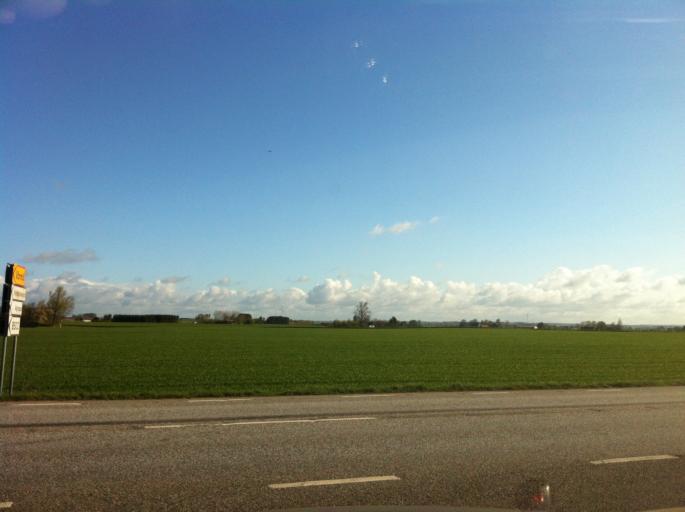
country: SE
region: Skane
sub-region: Svalovs Kommun
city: Teckomatorp
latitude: 55.8751
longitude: 13.0364
